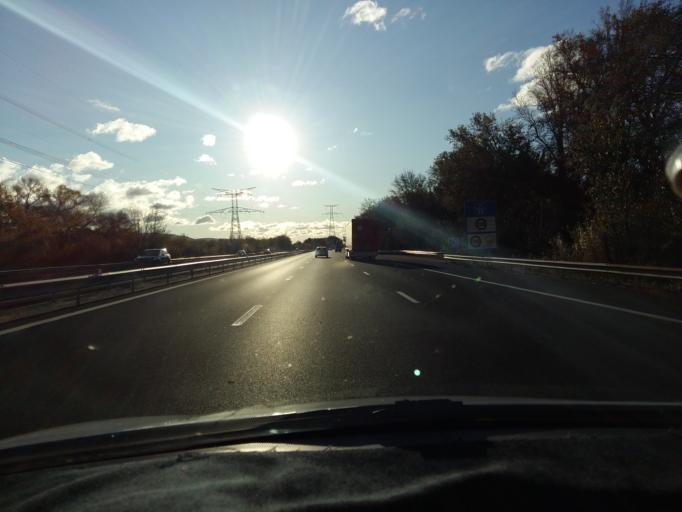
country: FR
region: Provence-Alpes-Cote d'Azur
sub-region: Departement des Bouches-du-Rhone
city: Cabannes
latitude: 43.8552
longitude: 4.9816
